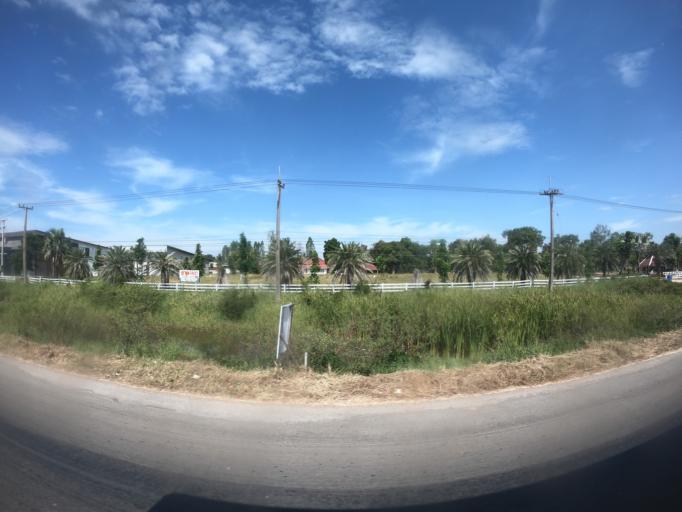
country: TH
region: Khon Kaen
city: Khon Kaen
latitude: 16.4161
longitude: 102.9099
